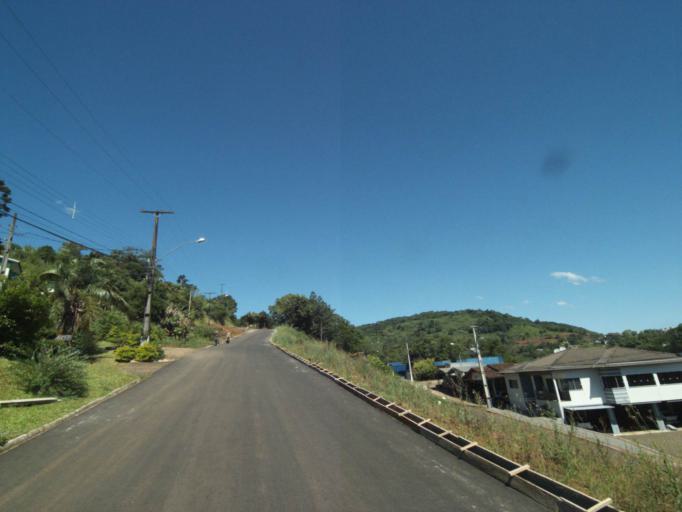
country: BR
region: Parana
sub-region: Ampere
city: Ampere
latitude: -26.1738
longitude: -53.3585
